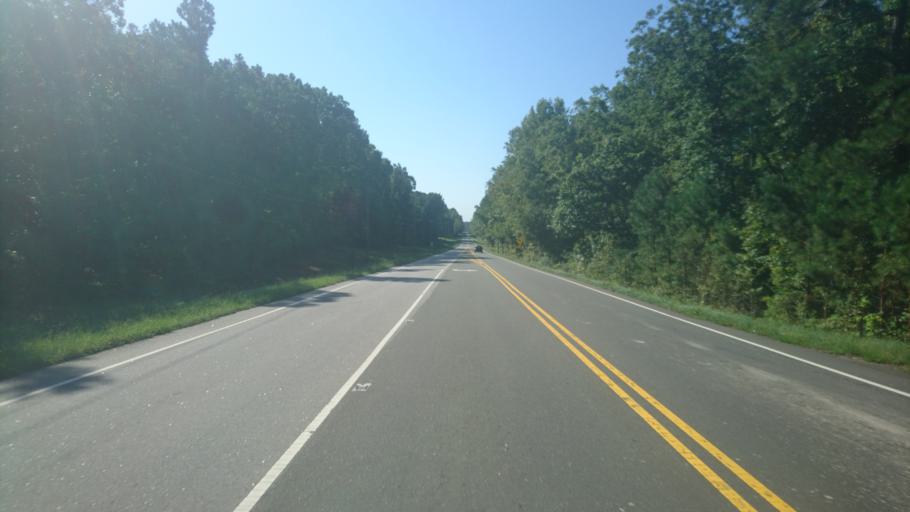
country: US
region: North Carolina
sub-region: Orange County
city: Hillsborough
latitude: 36.0372
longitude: -79.0820
